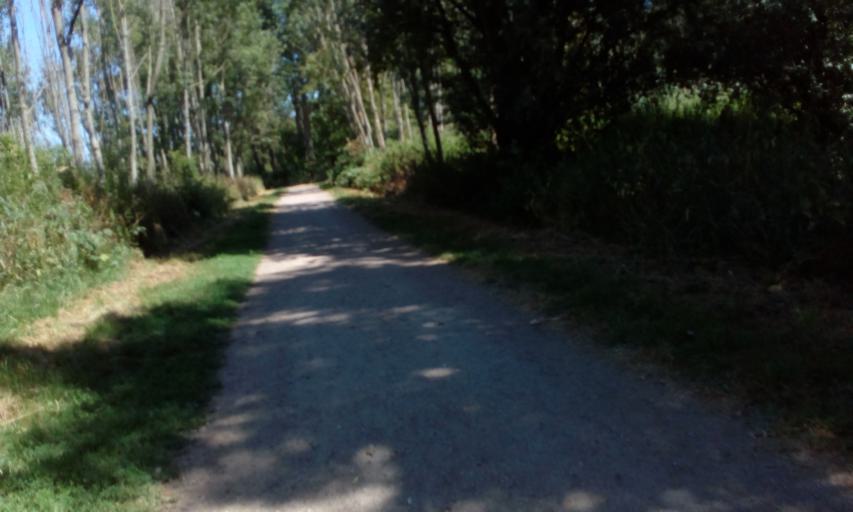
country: NL
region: South Holland
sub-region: Gemeente Pijnacker-Nootdorp
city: Pijnacker
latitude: 52.0311
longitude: 4.4072
